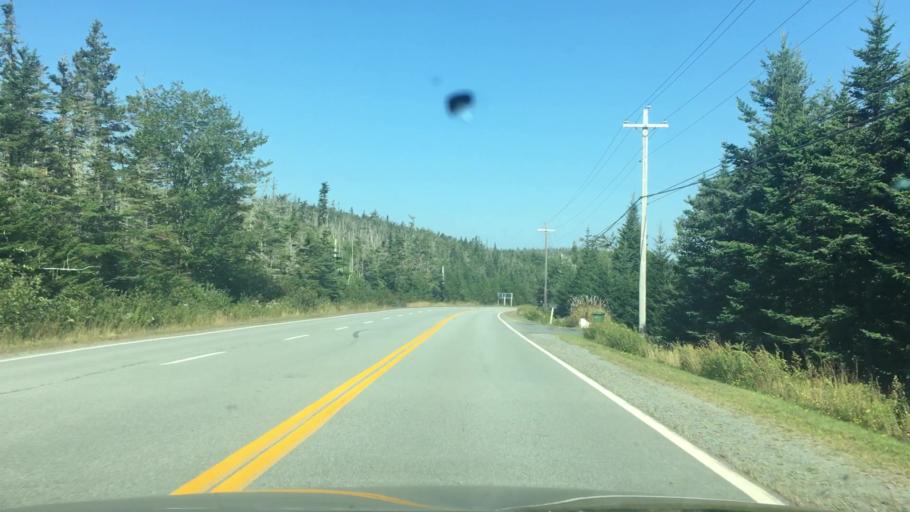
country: CA
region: Nova Scotia
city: New Glasgow
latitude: 44.8172
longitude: -62.6325
